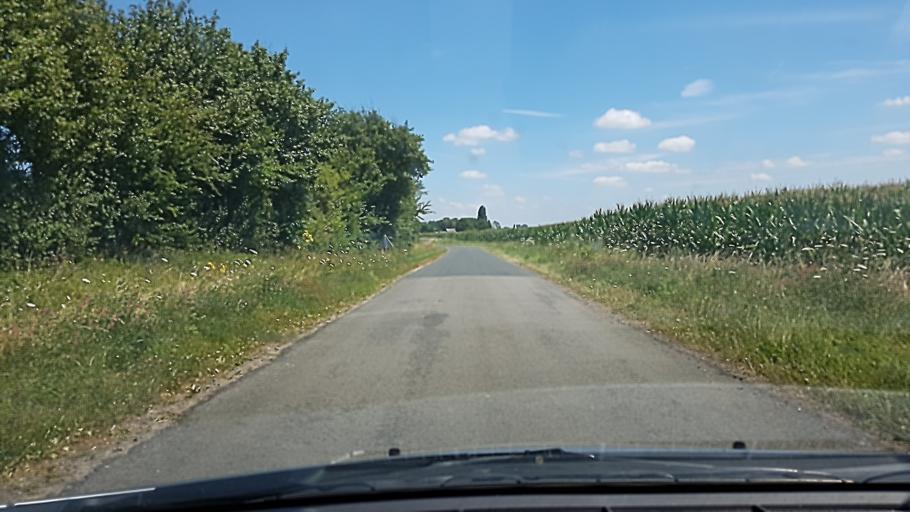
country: FR
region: Pays de la Loire
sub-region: Departement de Maine-et-Loire
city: Le Plessis-Grammoire
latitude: 47.5193
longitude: -0.4058
